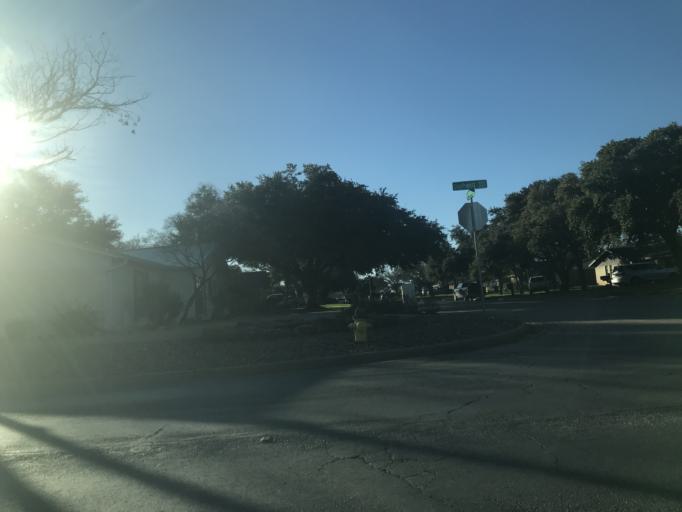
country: US
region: Texas
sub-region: Tom Green County
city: San Angelo
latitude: 31.4307
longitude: -100.4926
